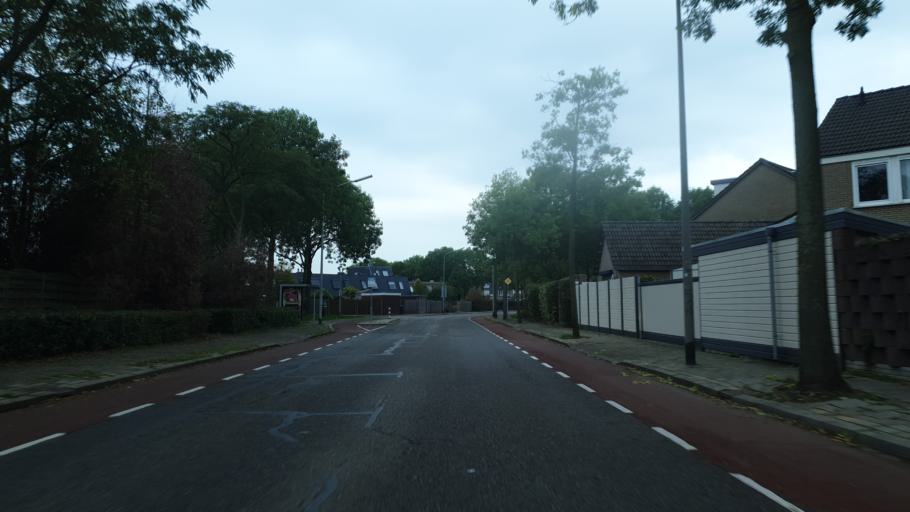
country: NL
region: Gelderland
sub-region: Gemeente Nijmegen
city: Lindenholt
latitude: 51.8196
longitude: 5.8062
